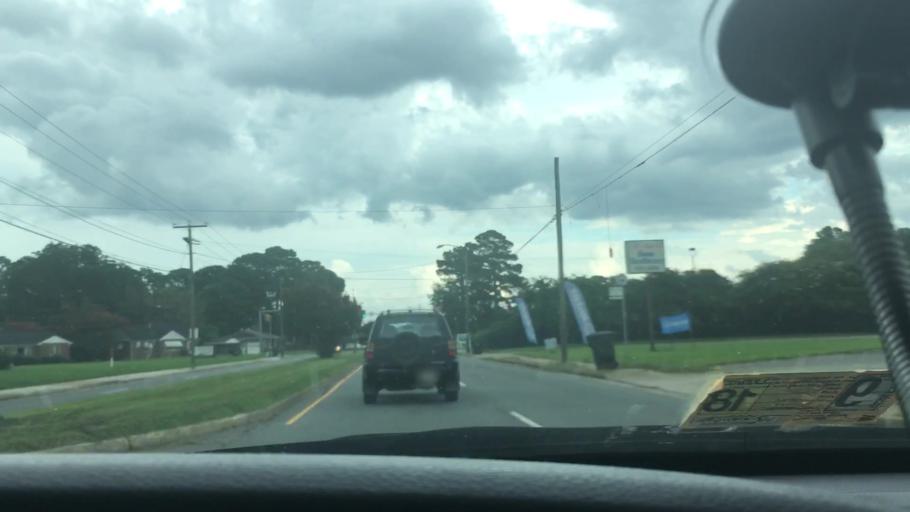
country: US
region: Virginia
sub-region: City of Portsmouth
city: Portsmouth Heights
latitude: 36.8208
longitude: -76.3872
